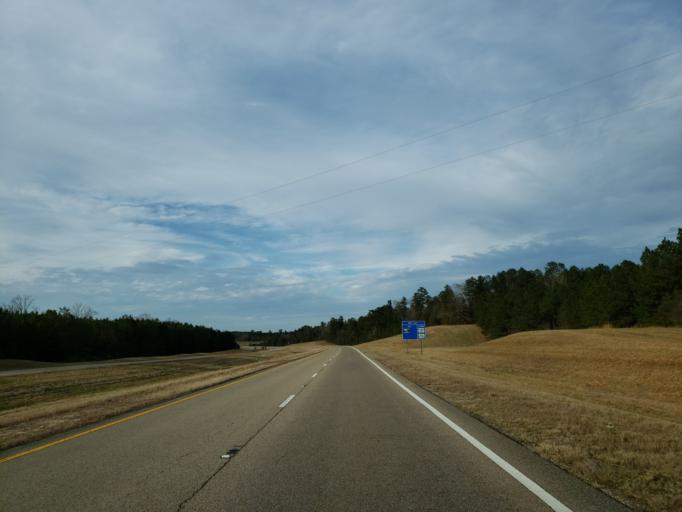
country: US
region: Mississippi
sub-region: Wayne County
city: Waynesboro
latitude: 31.6927
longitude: -88.6174
